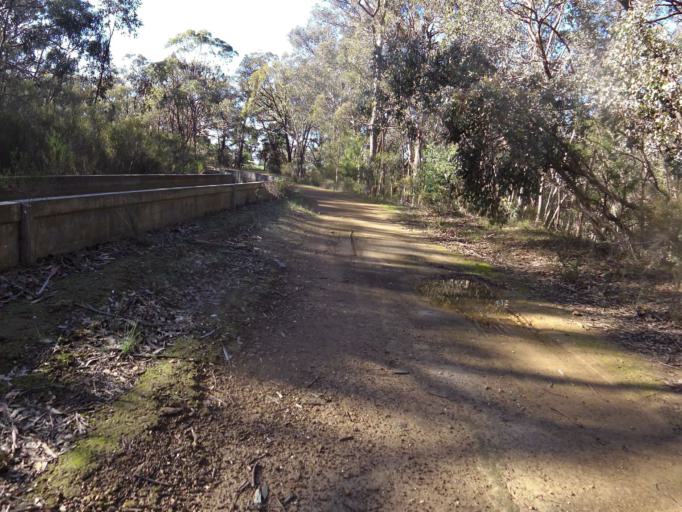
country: AU
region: Victoria
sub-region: Greater Bendigo
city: Kangaroo Flat
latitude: -36.8869
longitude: 144.2858
